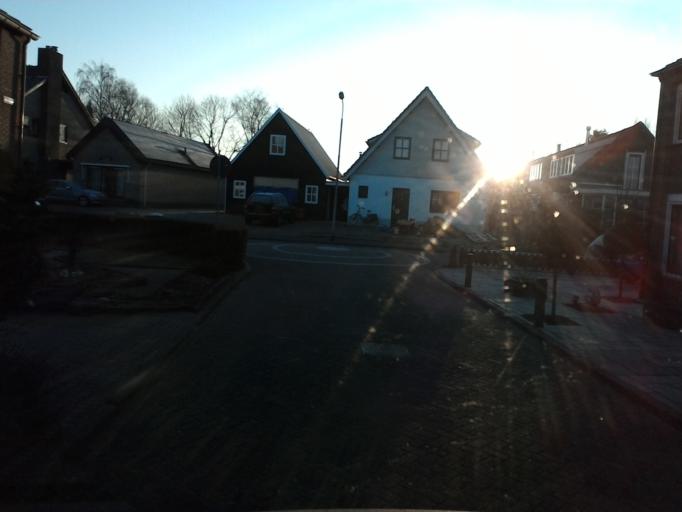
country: NL
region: South Holland
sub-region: Gemeente Giessenlanden
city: Giessenburg
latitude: 51.8435
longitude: 4.9268
